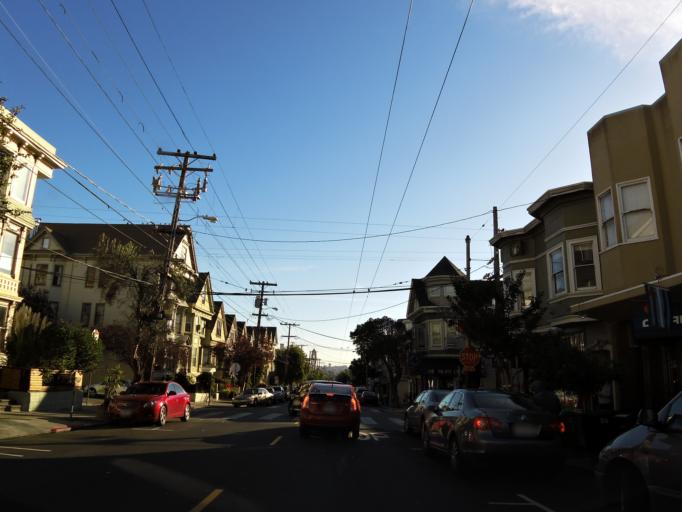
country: US
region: California
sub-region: San Francisco County
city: San Francisco
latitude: 37.7609
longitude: -122.4343
